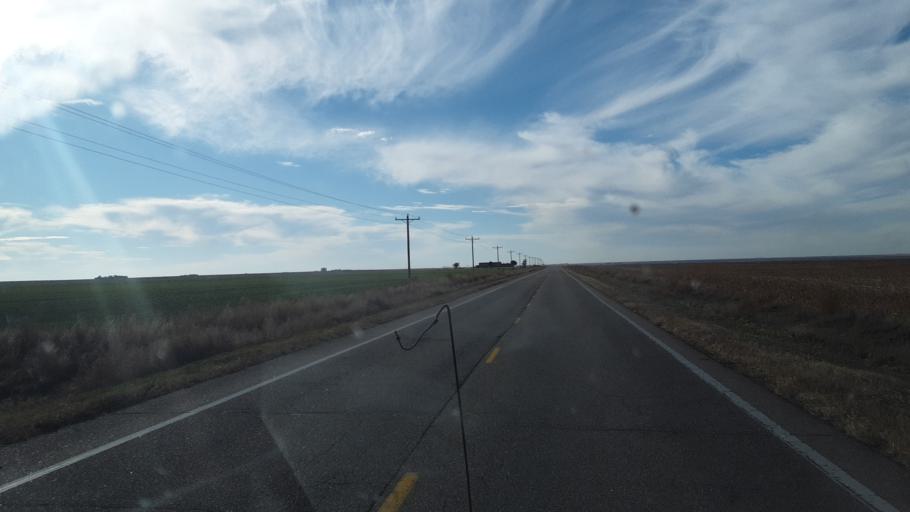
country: US
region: Kansas
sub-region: Gray County
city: Cimarron
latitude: 38.0591
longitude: -100.4913
